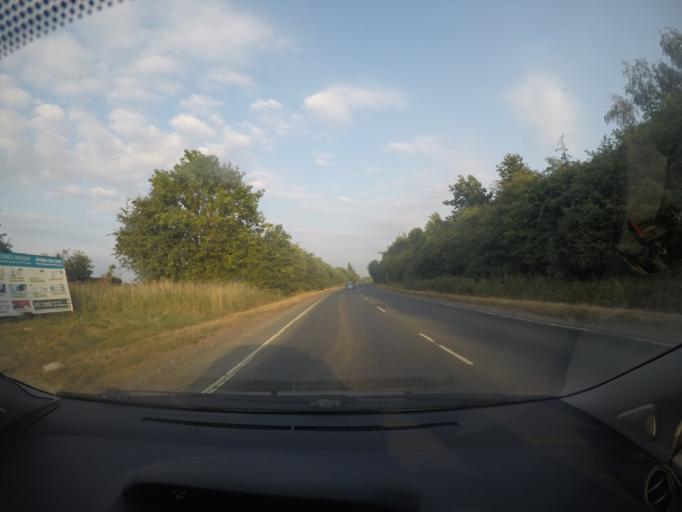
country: GB
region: England
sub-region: City of York
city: Huntington
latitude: 54.0038
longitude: -1.0522
